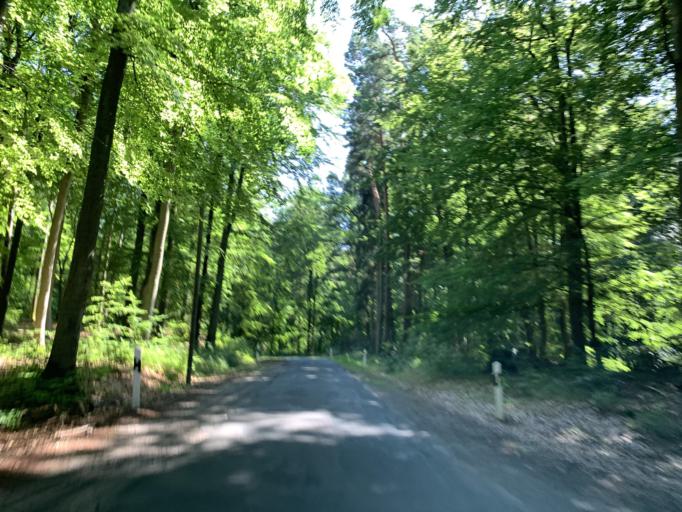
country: DE
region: Mecklenburg-Vorpommern
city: Carpin
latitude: 53.3167
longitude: 13.2508
